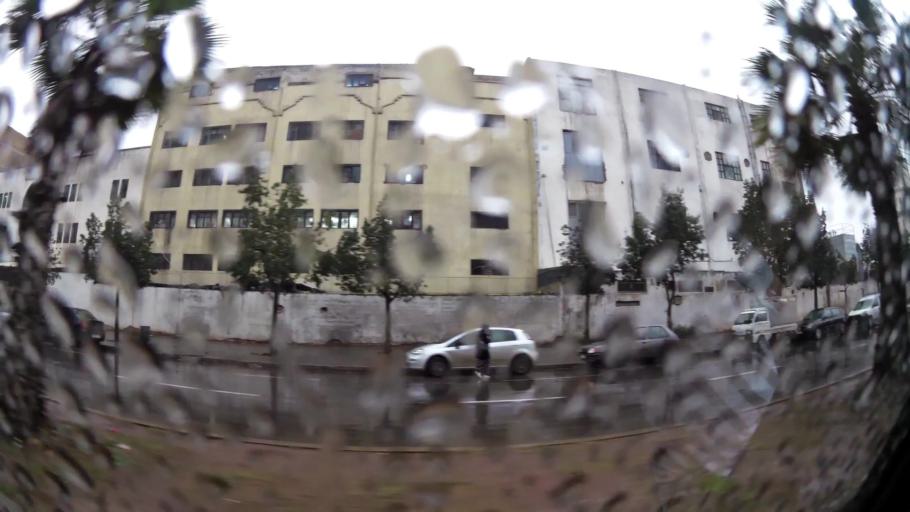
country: MA
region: Grand Casablanca
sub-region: Mediouna
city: Tit Mellil
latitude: 33.5676
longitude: -7.5261
